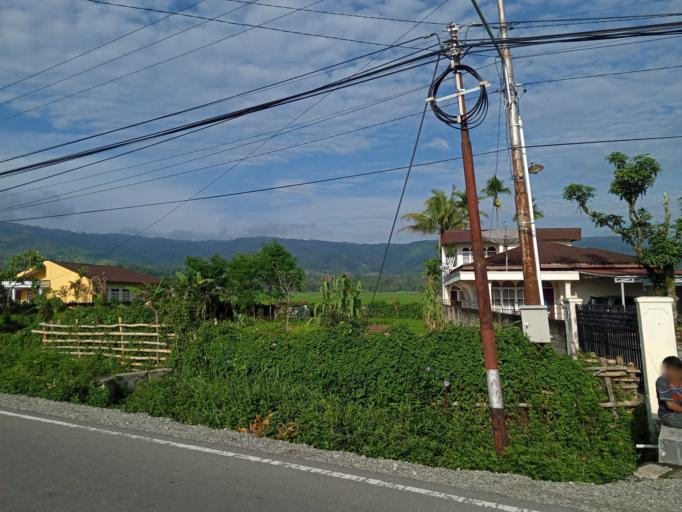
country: ID
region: Jambi
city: Semurup
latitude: -2.0044
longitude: 101.3768
